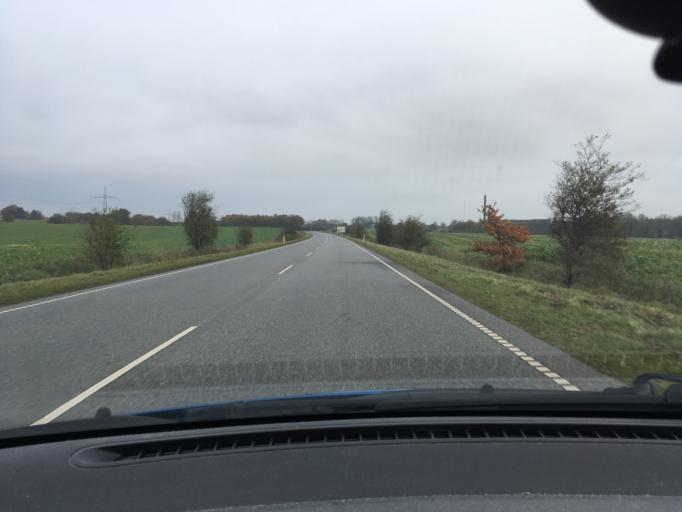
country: DK
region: South Denmark
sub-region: Aabenraa Kommune
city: Aabenraa
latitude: 54.9988
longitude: 9.4159
